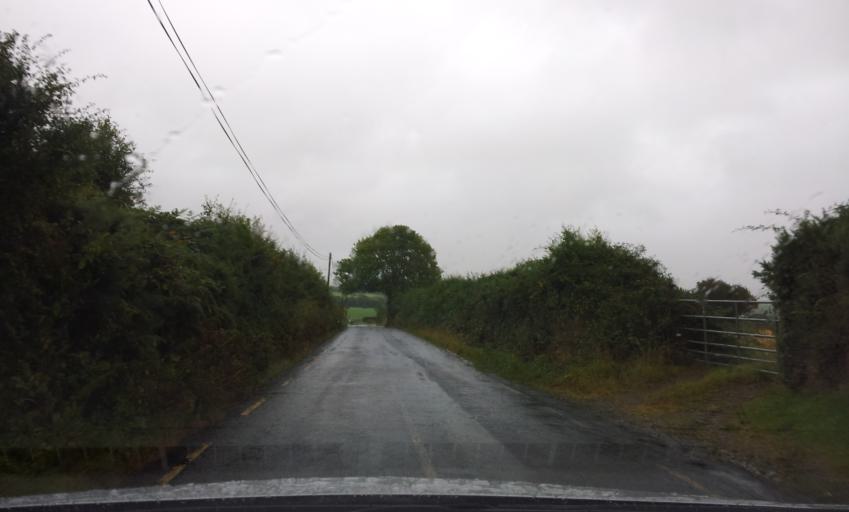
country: IE
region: Leinster
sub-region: Loch Garman
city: New Ross
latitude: 52.4091
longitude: -7.0183
